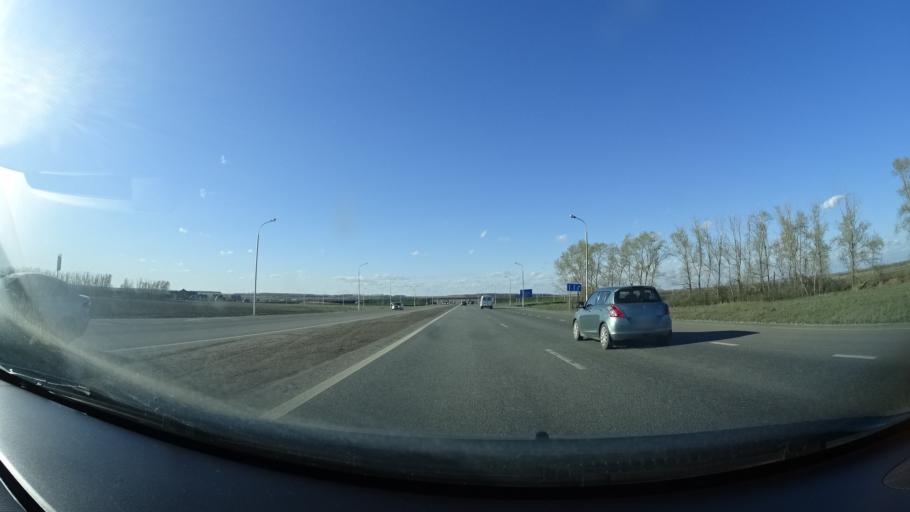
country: RU
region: Bashkortostan
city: Kabakovo
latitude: 54.4885
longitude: 55.9072
